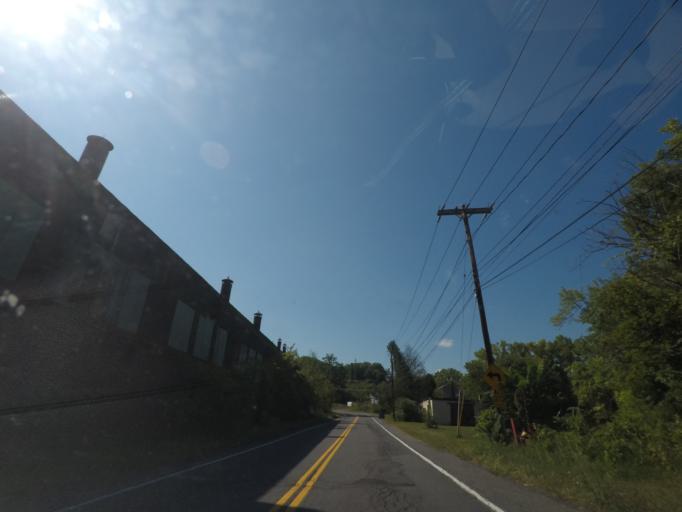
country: US
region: New York
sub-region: Albany County
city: Menands
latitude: 42.7150
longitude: -73.7210
